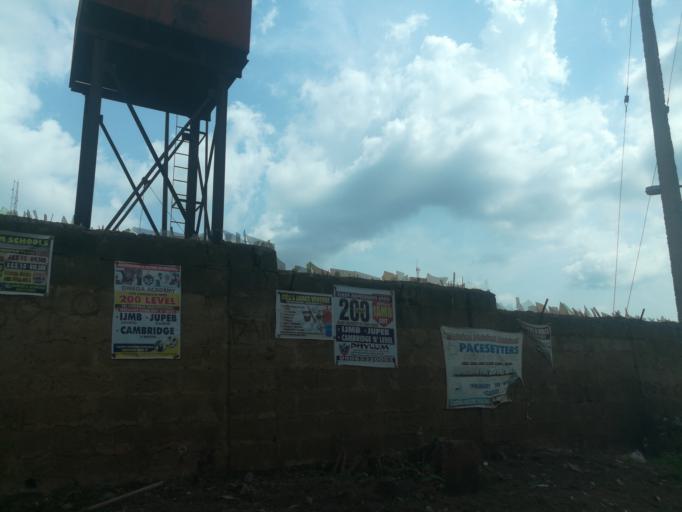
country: NG
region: Oyo
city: Ibadan
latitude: 7.3465
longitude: 3.8762
